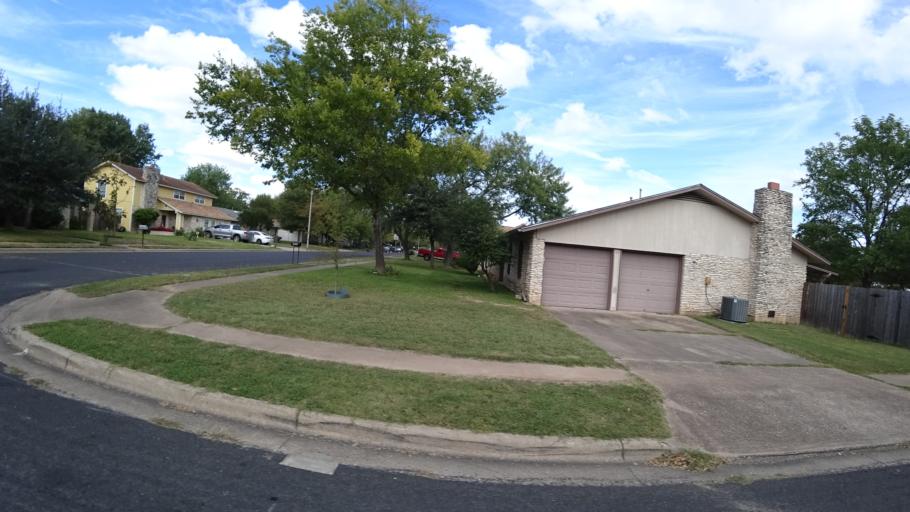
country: US
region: Texas
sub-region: Travis County
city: Austin
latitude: 30.1984
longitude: -97.7410
